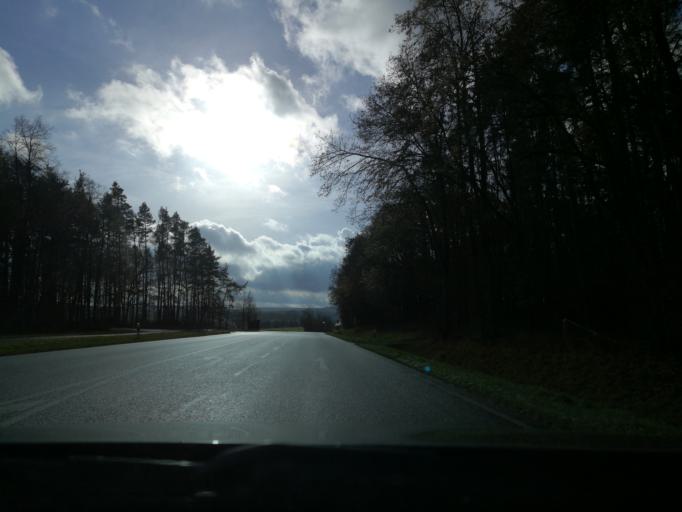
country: DE
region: Bavaria
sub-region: Regierungsbezirk Mittelfranken
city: Spalt
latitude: 49.2258
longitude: 10.8916
